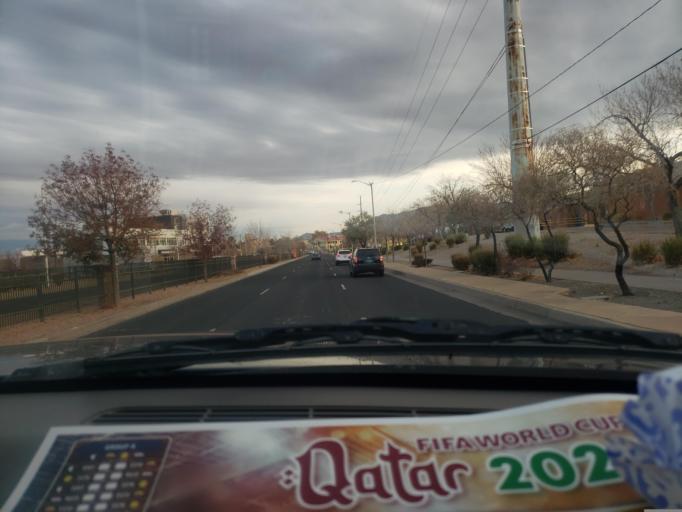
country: US
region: New Mexico
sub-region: Bernalillo County
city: Albuquerque
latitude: 35.0735
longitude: -106.6294
